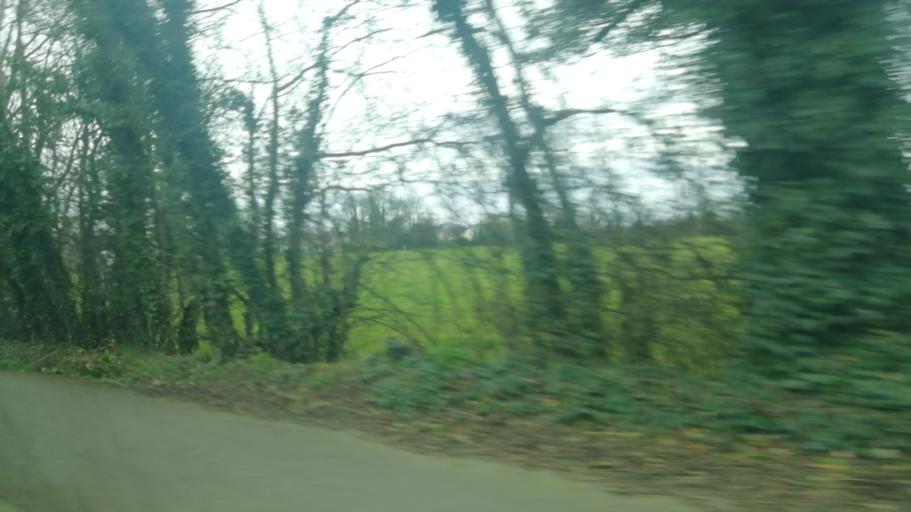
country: IE
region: Leinster
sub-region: Kildare
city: Derrinturn
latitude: 53.3450
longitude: -6.9494
